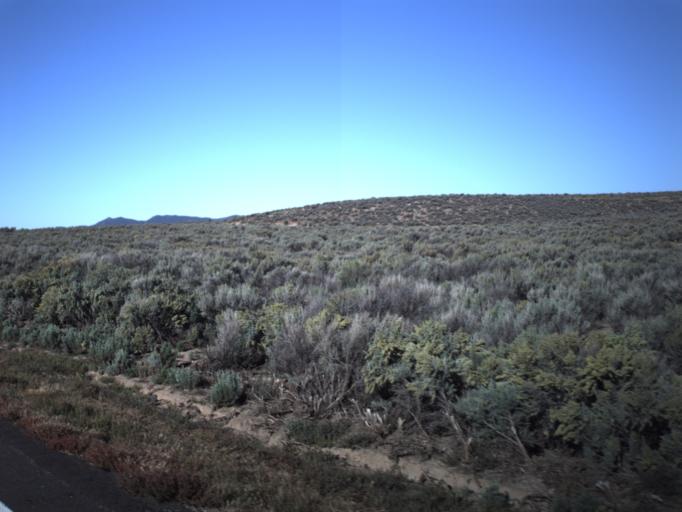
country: US
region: Utah
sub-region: Washington County
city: Enterprise
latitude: 37.7904
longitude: -113.9501
